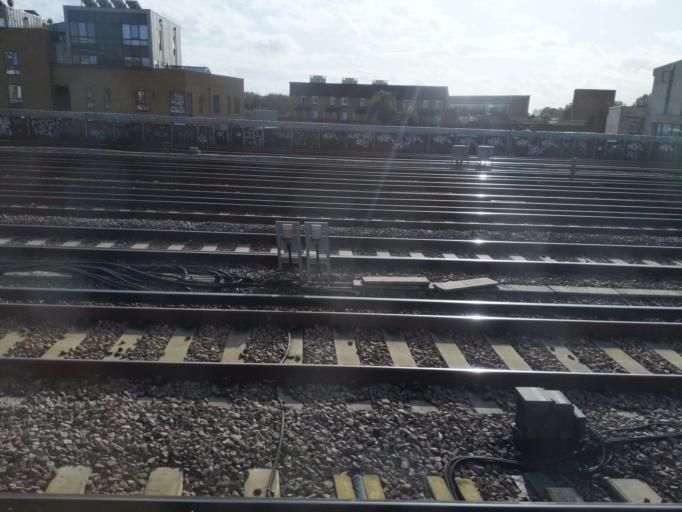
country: GB
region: England
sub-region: Greater London
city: Bethnal Green
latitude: 51.4935
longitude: -0.0626
